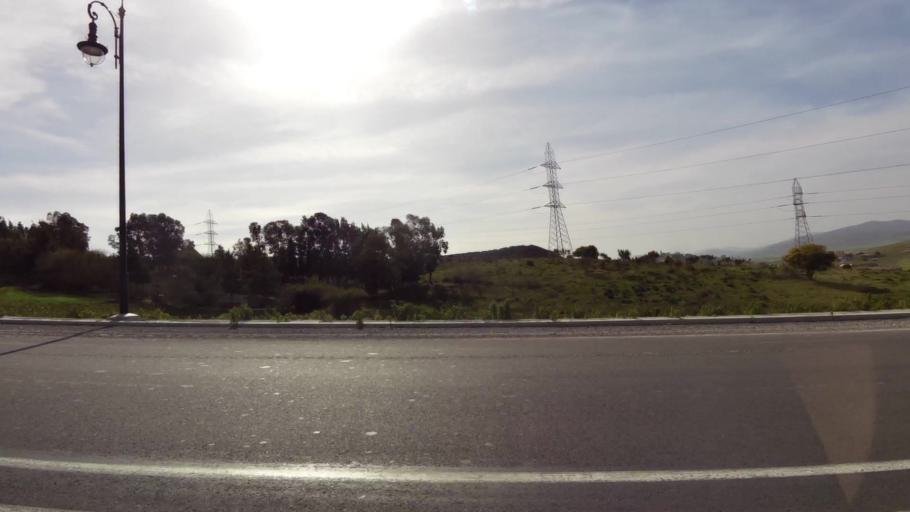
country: MA
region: Tanger-Tetouan
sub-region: Tanger-Assilah
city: Tangier
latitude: 35.7021
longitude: -5.7956
